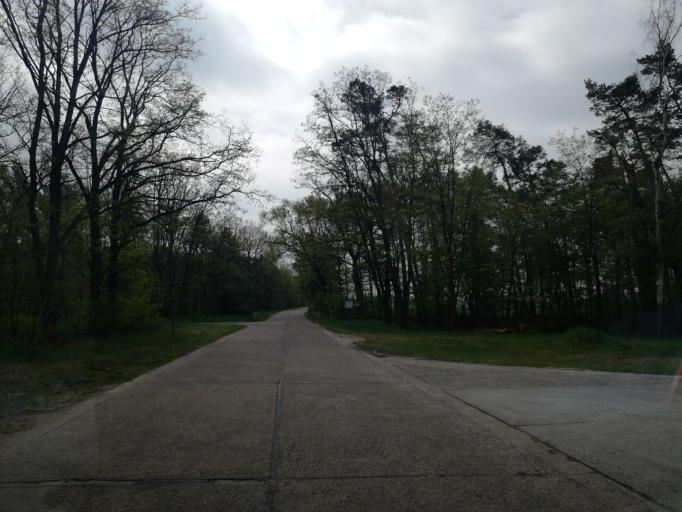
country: DE
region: Saxony
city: Beilrode
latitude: 51.6556
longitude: 13.1132
